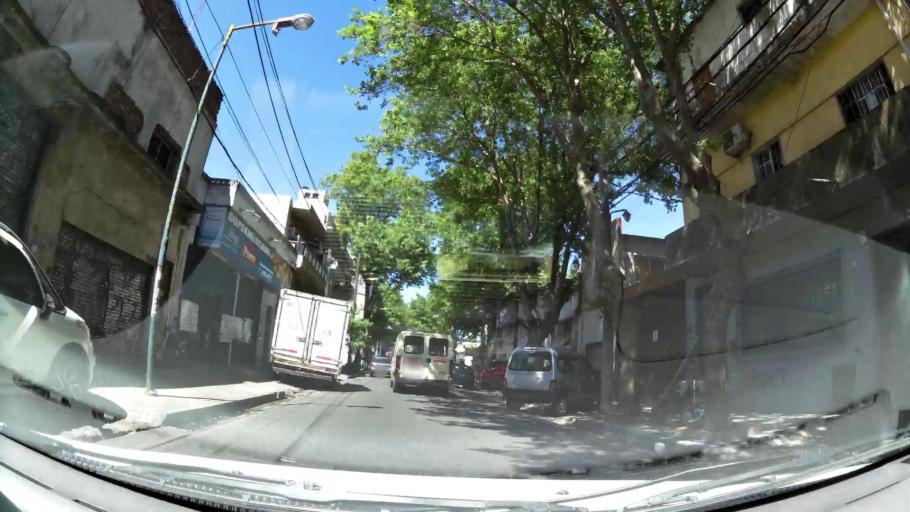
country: AR
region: Buenos Aires
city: Caseros
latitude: -34.5872
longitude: -58.5507
